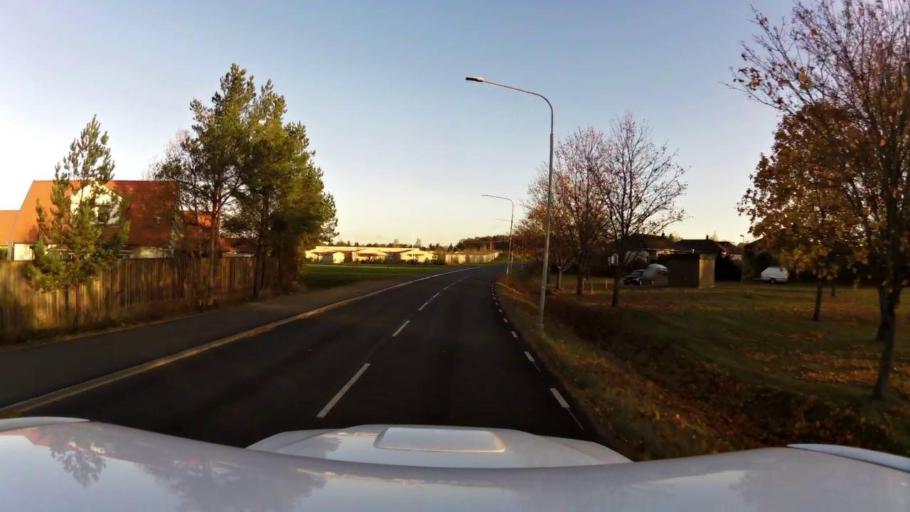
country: SE
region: OEstergoetland
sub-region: Linkopings Kommun
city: Ekangen
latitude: 58.4304
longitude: 15.6767
